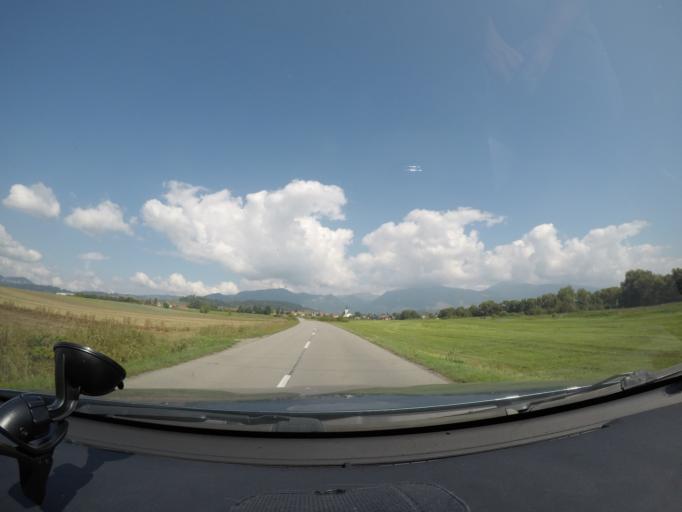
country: SK
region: Zilinsky
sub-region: Okres Liptovsky Mikulas
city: Liptovsky Mikulas
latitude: 49.1098
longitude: 19.6013
